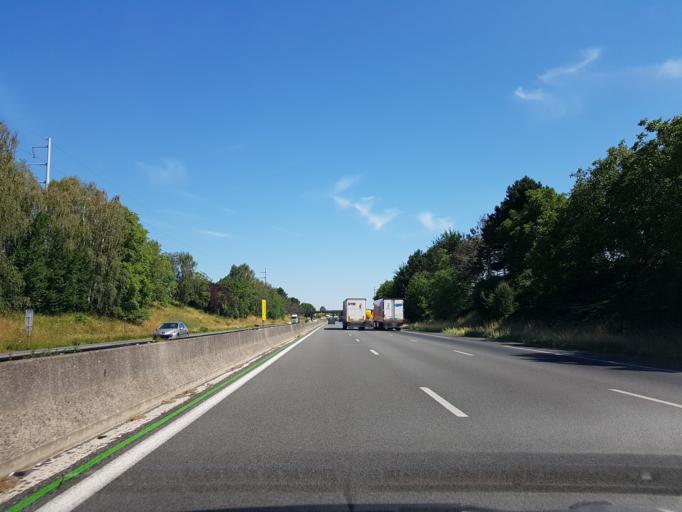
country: FR
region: Picardie
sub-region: Departement de l'Oise
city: Remy
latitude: 49.4407
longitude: 2.6964
